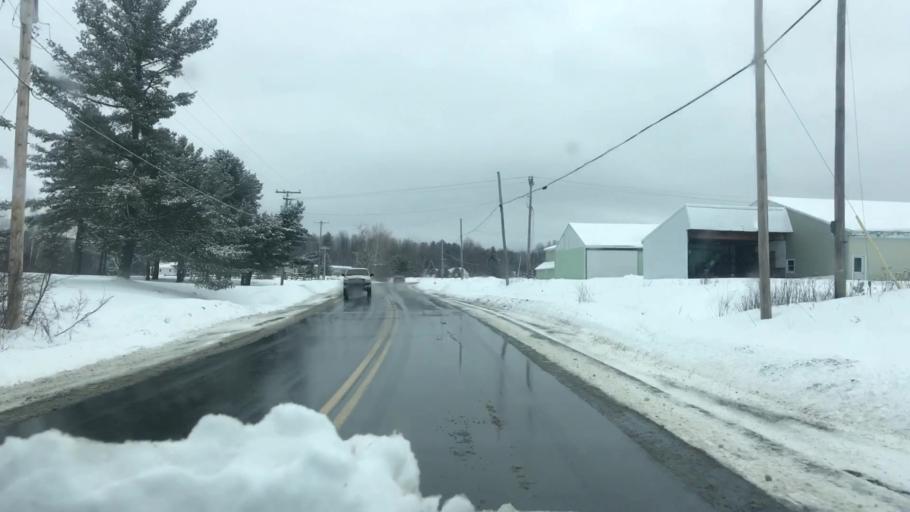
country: US
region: Maine
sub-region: Penobscot County
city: Charleston
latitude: 44.9975
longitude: -69.0368
